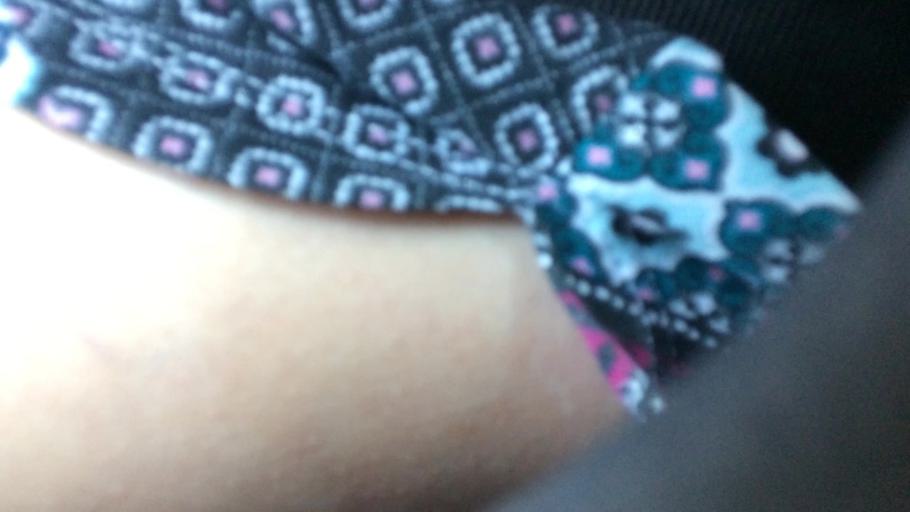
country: US
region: New Mexico
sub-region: San Miguel County
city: Las Vegas
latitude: 35.8480
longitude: -104.9336
